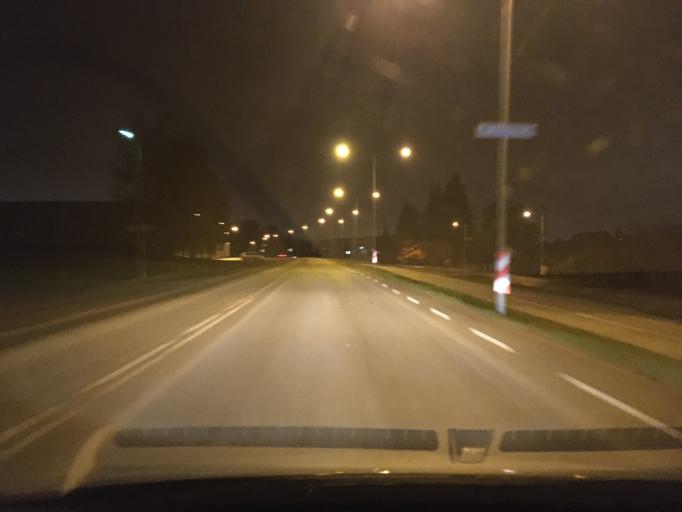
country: EE
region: Tartu
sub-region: Tartu linn
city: Tartu
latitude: 58.4012
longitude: 26.7083
